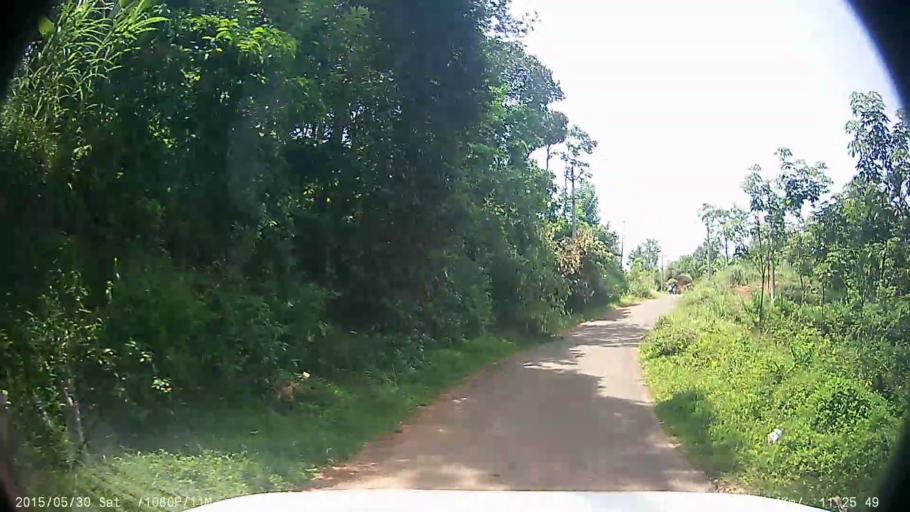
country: IN
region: Kerala
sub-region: Wayanad
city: Panamaram
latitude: 11.8117
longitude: 76.0333
